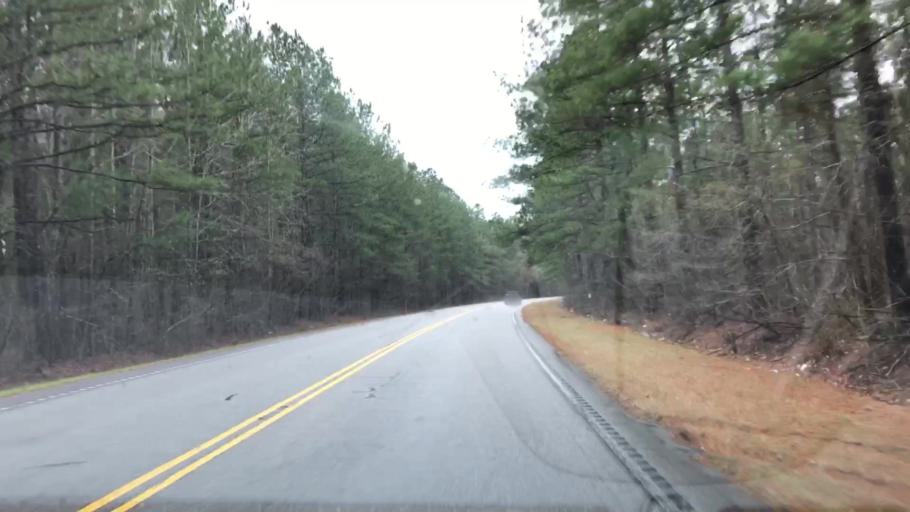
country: US
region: South Carolina
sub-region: Williamsburg County
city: Andrews
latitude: 33.5197
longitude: -79.4938
